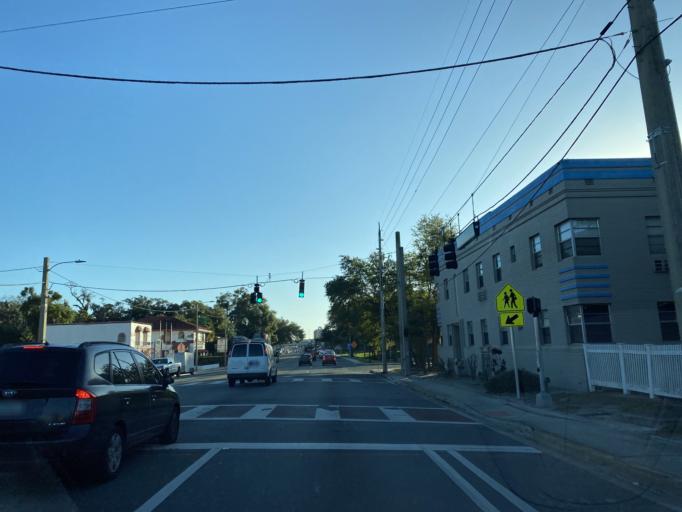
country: US
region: Florida
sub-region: Orange County
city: Orlando
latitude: 28.5530
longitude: -81.3879
